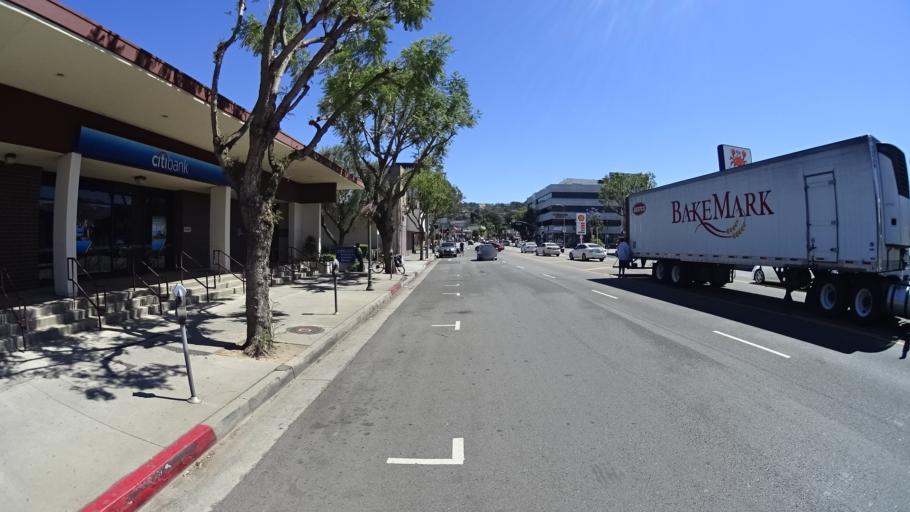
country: US
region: California
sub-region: Los Angeles County
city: Sherman Oaks
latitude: 34.1529
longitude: -118.4486
